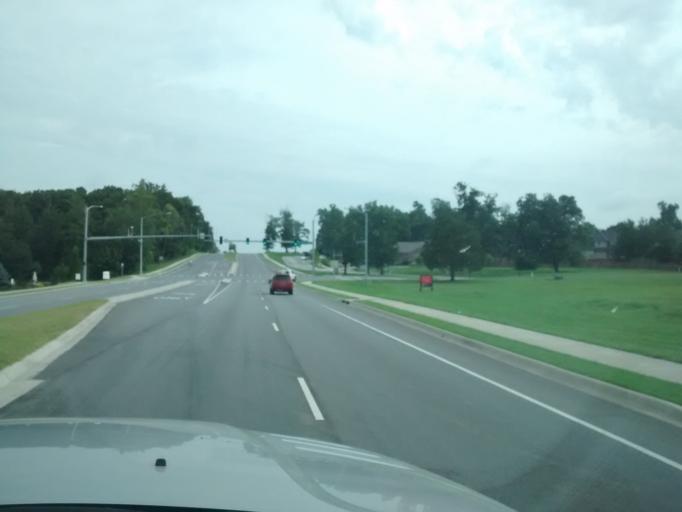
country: US
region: Arkansas
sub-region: Washington County
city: Johnson
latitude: 36.1352
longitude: -94.1178
